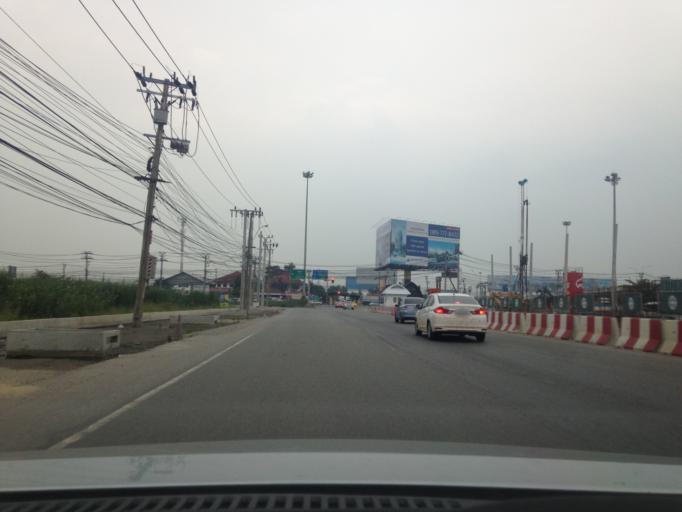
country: TH
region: Bangkok
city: Lat Krabang
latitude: 13.7309
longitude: 100.7449
